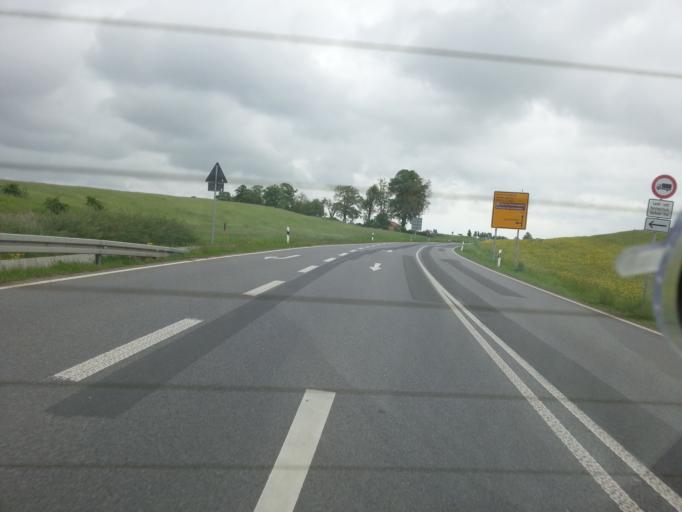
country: DE
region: Mecklenburg-Vorpommern
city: Malchow
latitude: 53.4705
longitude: 12.4430
